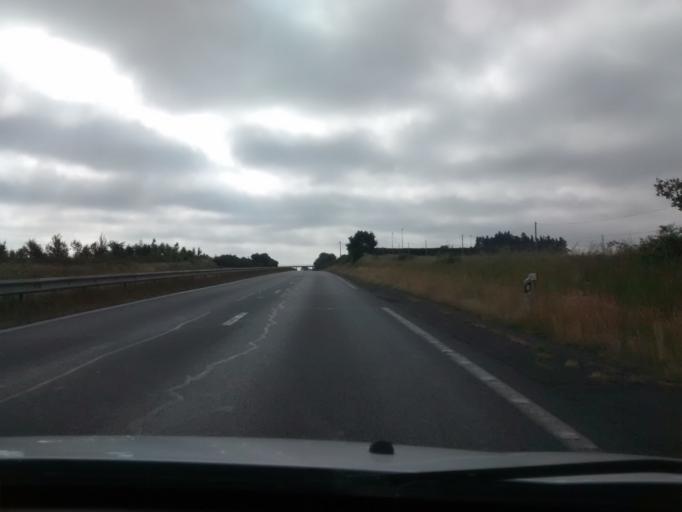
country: FR
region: Brittany
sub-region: Departement d'Ille-et-Vilaine
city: Saint-Didier
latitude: 48.0908
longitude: -1.3816
